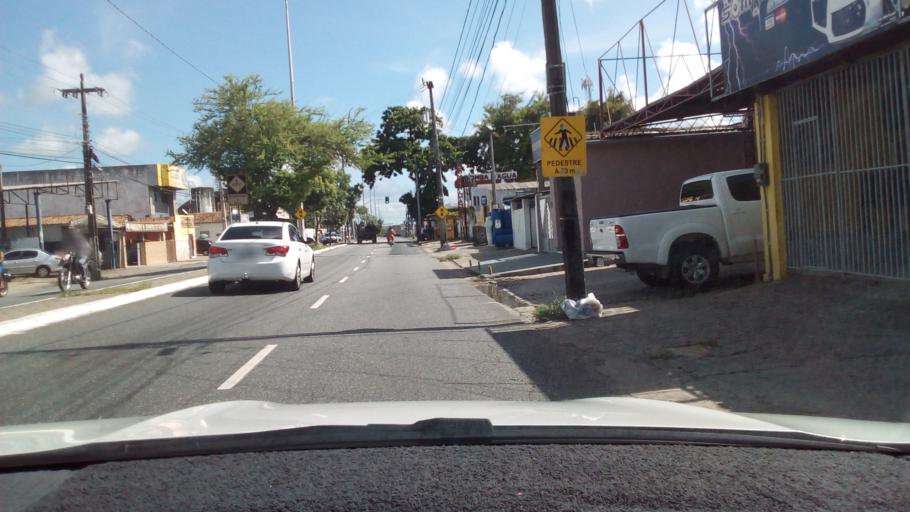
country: BR
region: Paraiba
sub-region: Joao Pessoa
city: Joao Pessoa
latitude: -7.1484
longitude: -34.8933
